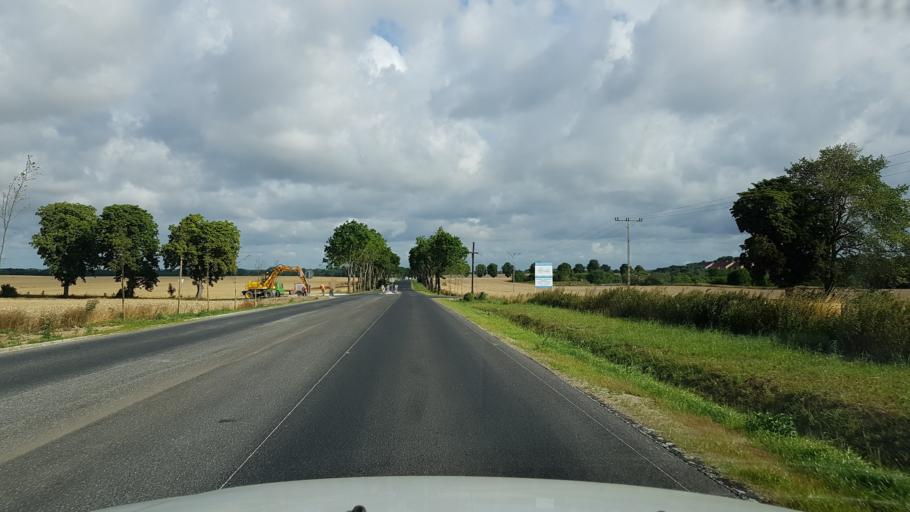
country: PL
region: West Pomeranian Voivodeship
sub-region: Powiat gryficki
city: Ploty
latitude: 53.8406
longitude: 15.2371
